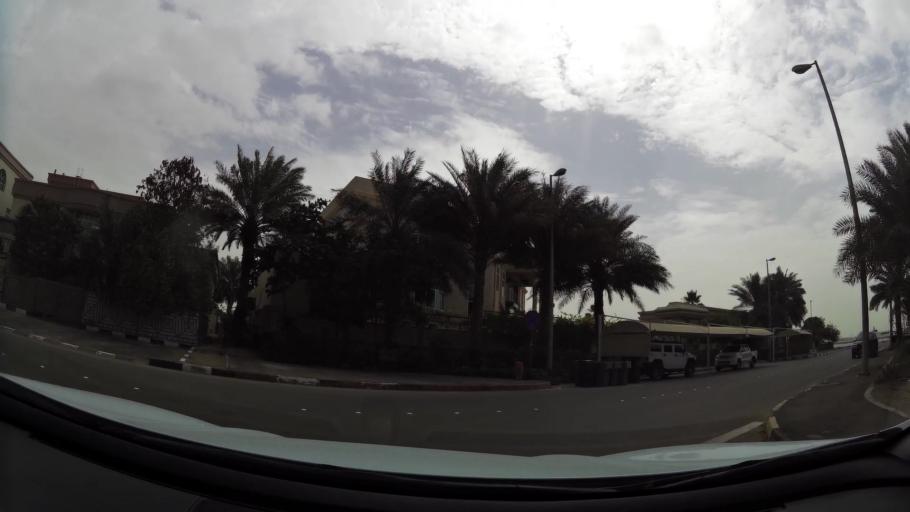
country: AE
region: Abu Dhabi
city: Abu Dhabi
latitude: 24.3932
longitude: 54.5046
